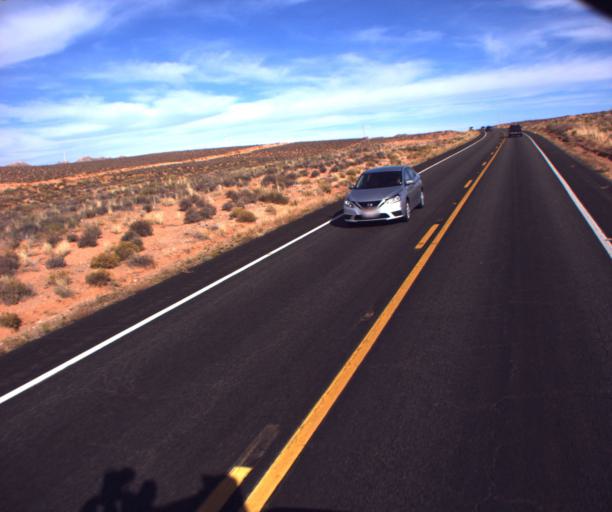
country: US
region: Arizona
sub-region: Apache County
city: Many Farms
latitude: 36.9252
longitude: -109.5923
